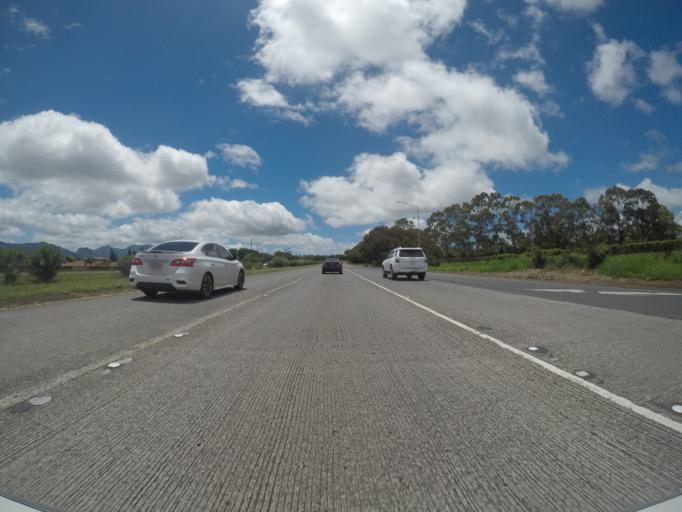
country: US
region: Hawaii
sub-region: Honolulu County
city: Waipi'o Acres
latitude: 21.4692
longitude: -158.0072
